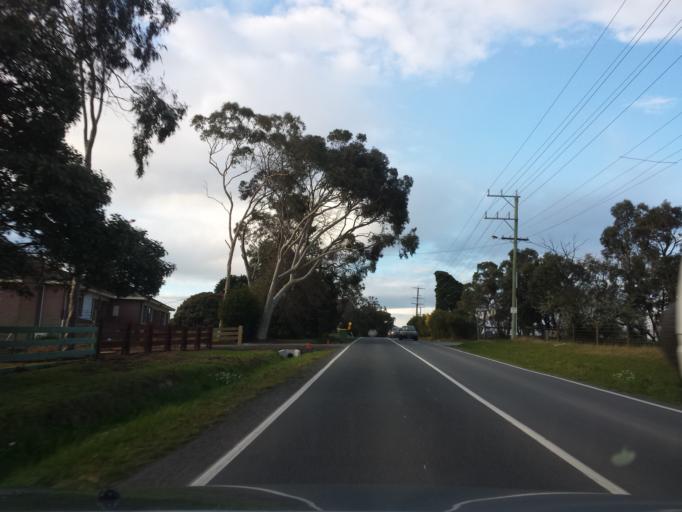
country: AU
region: Victoria
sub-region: Yarra Ranges
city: Belgrave South
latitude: -37.9422
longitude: 145.3558
